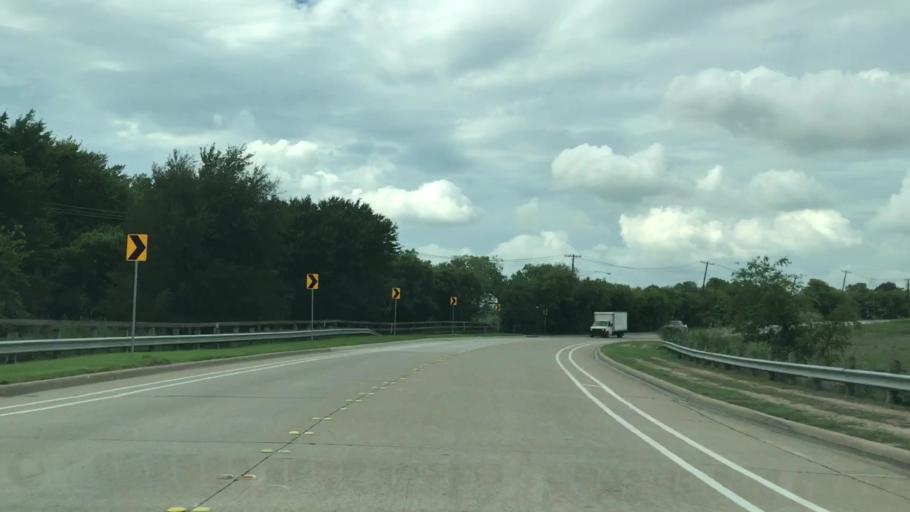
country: US
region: Texas
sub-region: Collin County
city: Frisco
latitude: 33.1425
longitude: -96.8250
